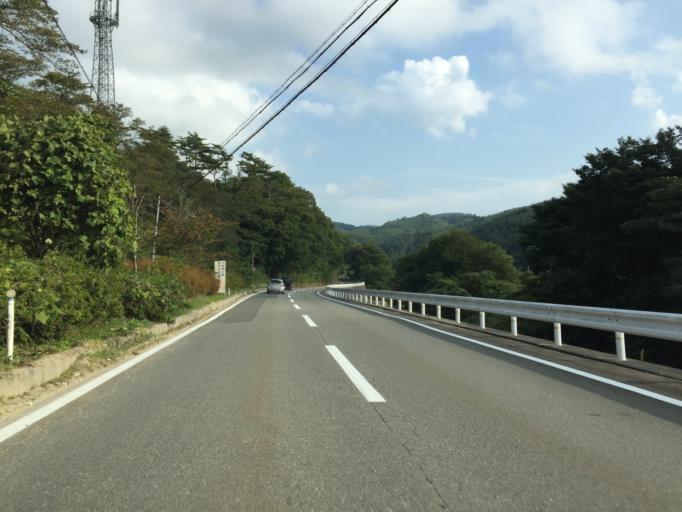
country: JP
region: Fukushima
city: Namie
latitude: 37.5668
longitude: 140.8013
